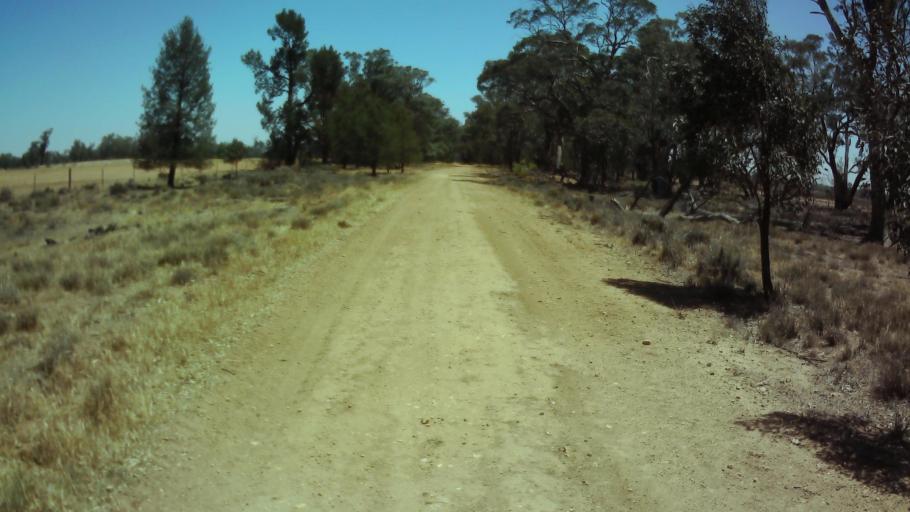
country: AU
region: New South Wales
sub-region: Weddin
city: Grenfell
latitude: -34.0394
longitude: 147.8503
